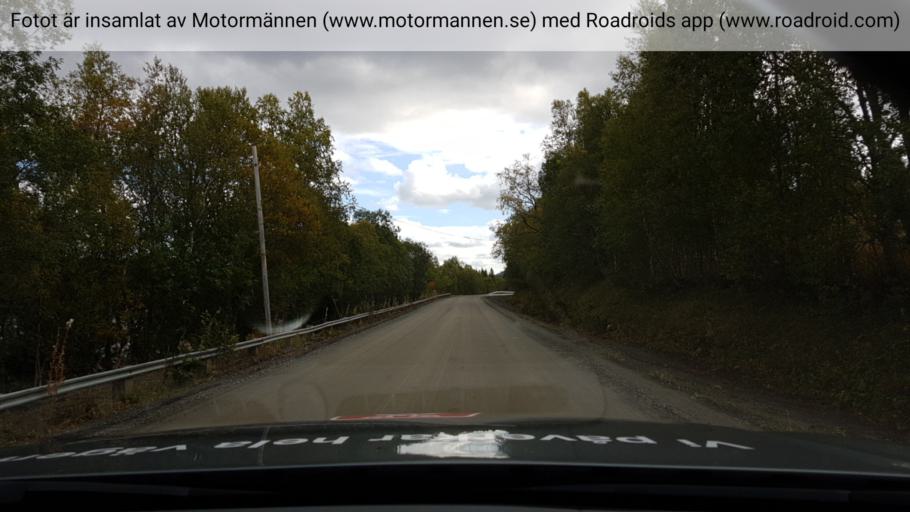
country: SE
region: Jaemtland
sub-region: Are Kommun
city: Are
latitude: 63.7116
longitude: 12.6319
